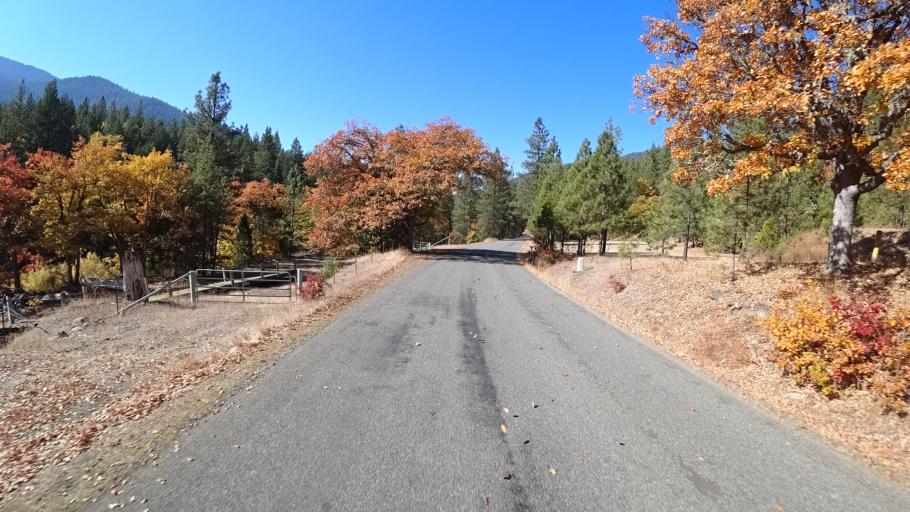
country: US
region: California
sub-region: Siskiyou County
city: Happy Camp
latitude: 41.6450
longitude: -123.0356
